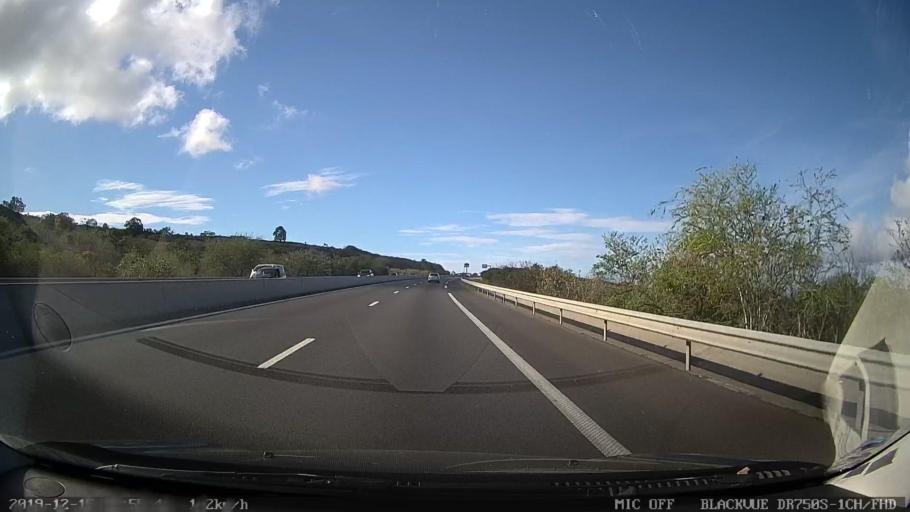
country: RE
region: Reunion
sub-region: Reunion
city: Saint-Paul
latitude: -21.0593
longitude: 55.2496
